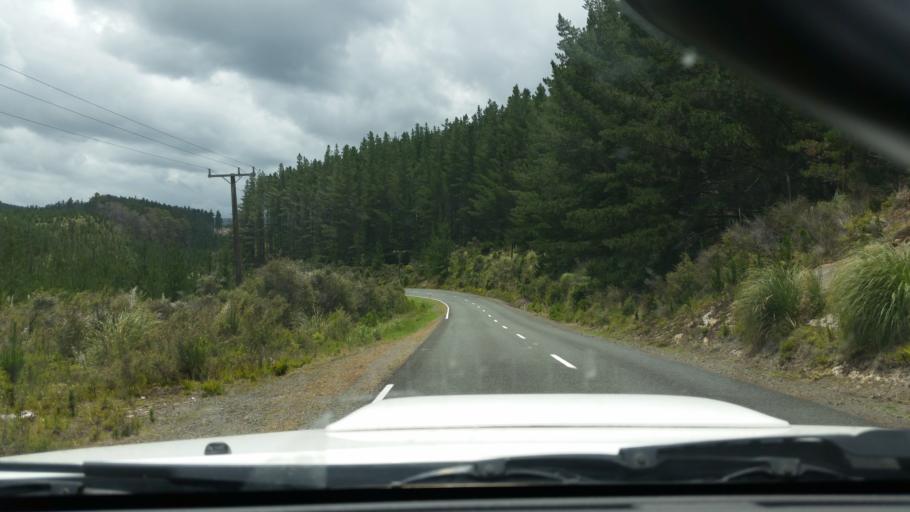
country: NZ
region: Northland
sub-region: Kaipara District
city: Dargaville
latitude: -35.8216
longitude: 173.7096
